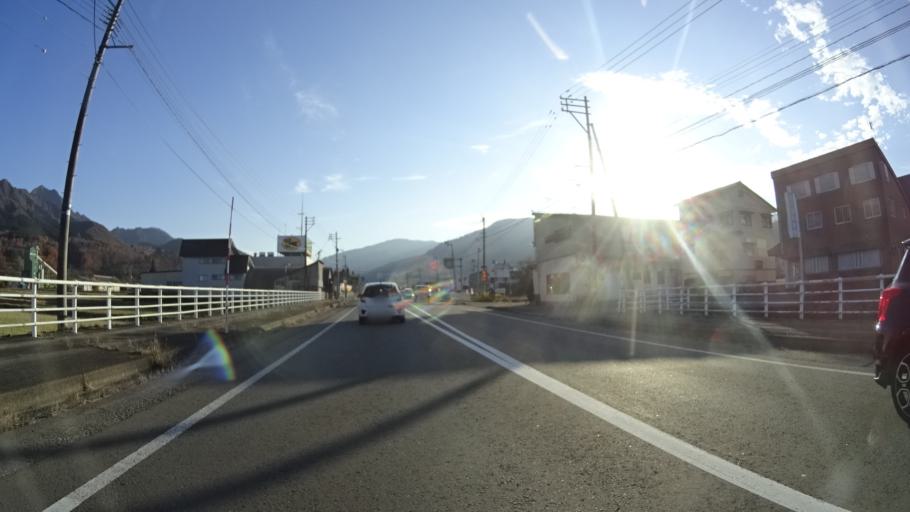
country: JP
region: Niigata
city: Shiozawa
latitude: 36.9874
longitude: 138.8088
